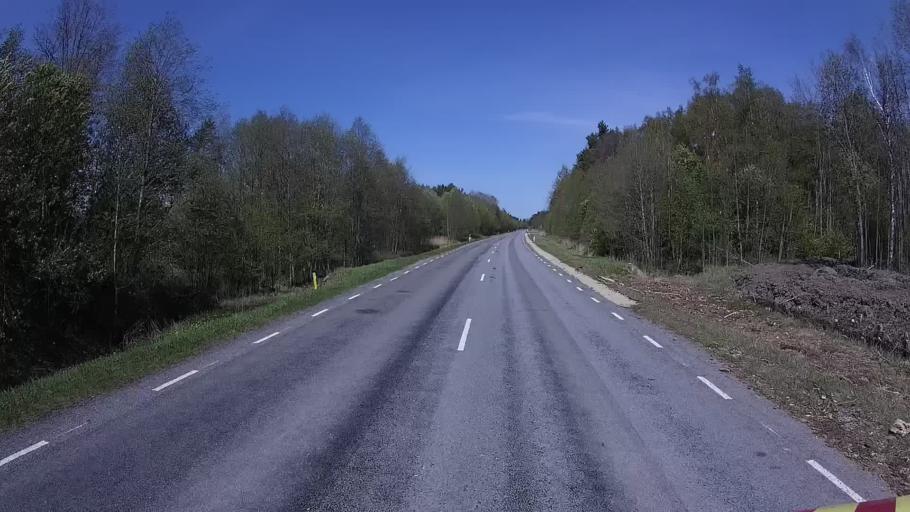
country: EE
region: Laeaene
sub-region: Ridala Parish
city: Uuemoisa
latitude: 58.8428
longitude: 23.6492
